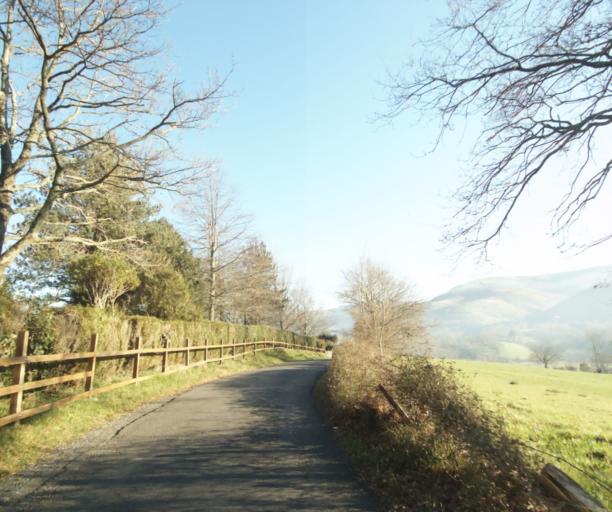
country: FR
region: Aquitaine
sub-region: Departement des Pyrenees-Atlantiques
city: Urrugne
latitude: 43.3496
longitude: -1.7073
